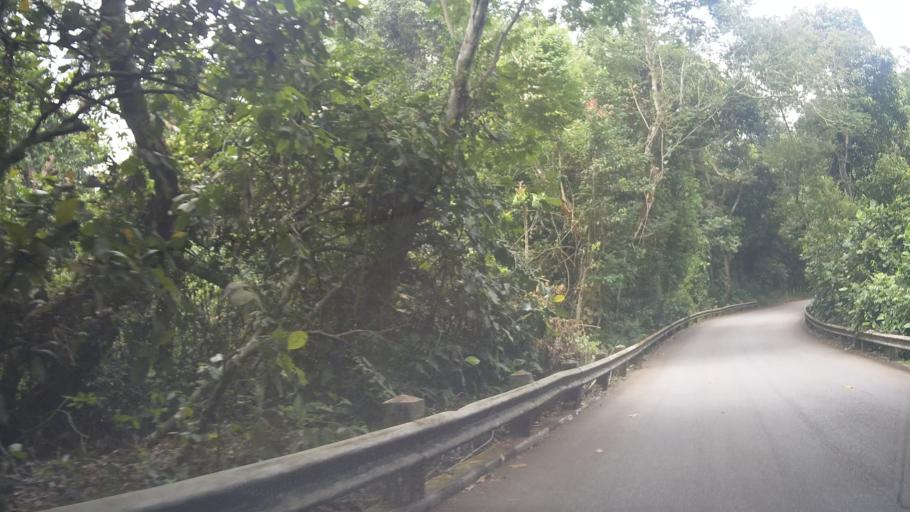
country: SG
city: Singapore
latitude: 1.3537
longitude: 103.7927
